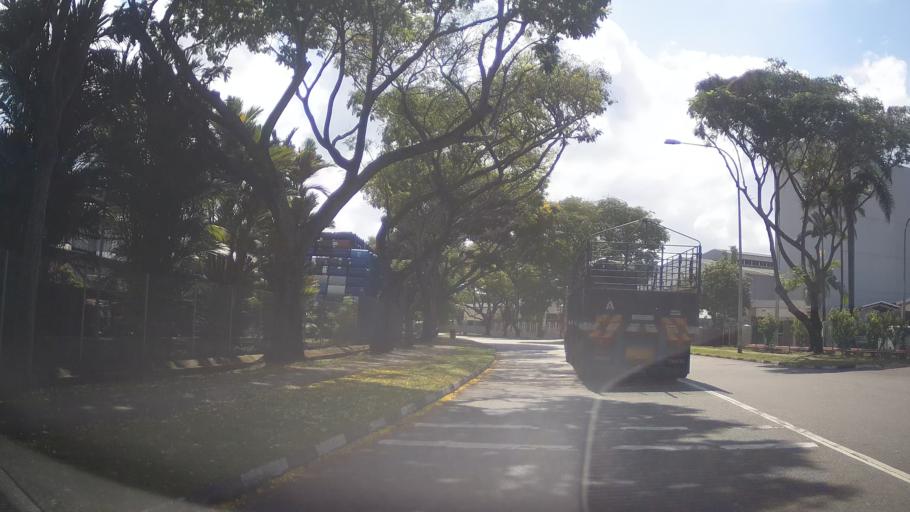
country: MY
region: Johor
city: Johor Bahru
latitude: 1.3096
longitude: 103.6636
